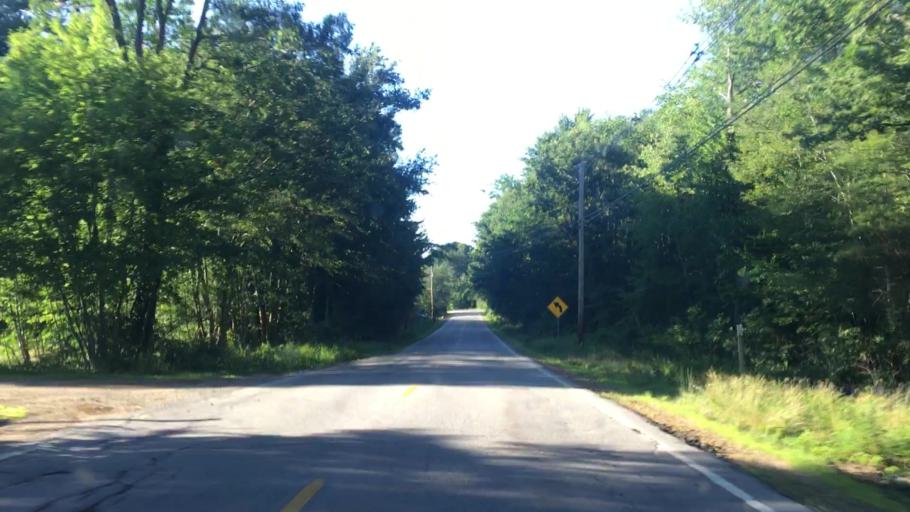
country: US
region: New Hampshire
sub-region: Rockingham County
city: Sandown
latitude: 42.9488
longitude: -71.1955
